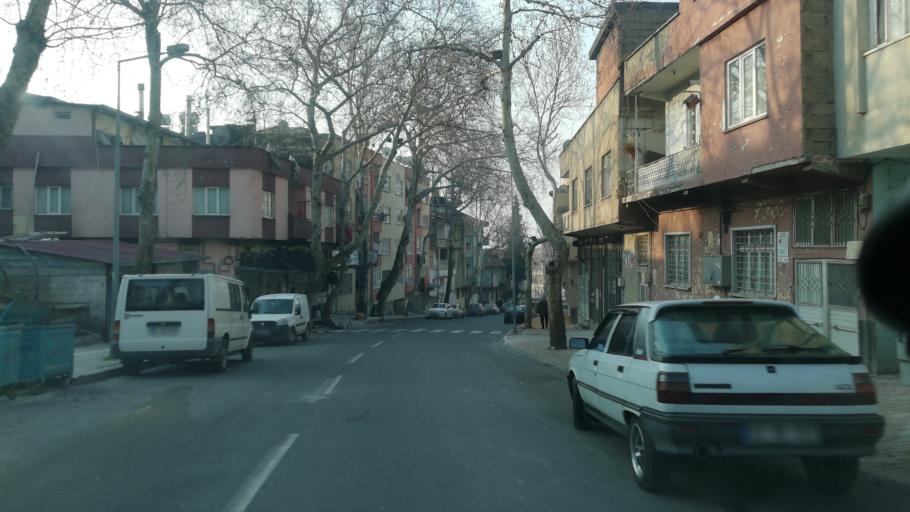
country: TR
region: Kahramanmaras
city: Kahramanmaras
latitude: 37.5911
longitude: 36.9271
